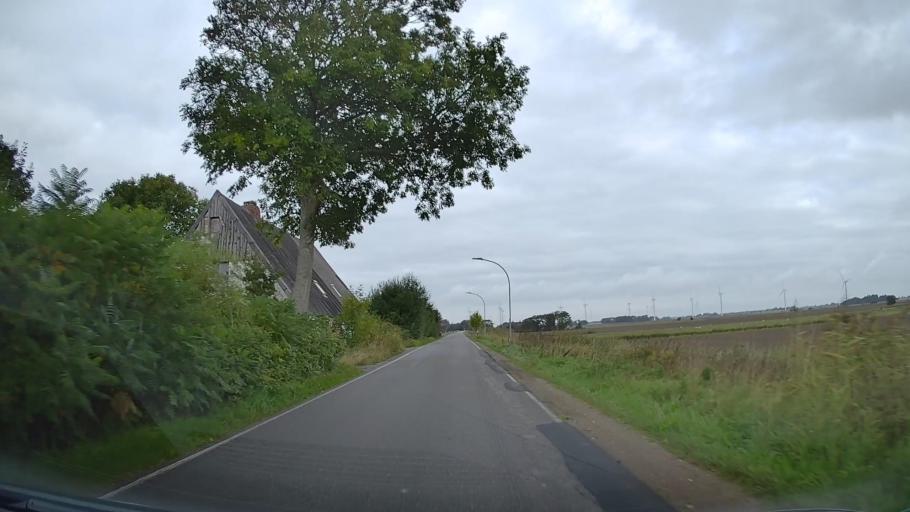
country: DE
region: Schleswig-Holstein
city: Galmsbull
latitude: 54.7784
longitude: 8.7324
